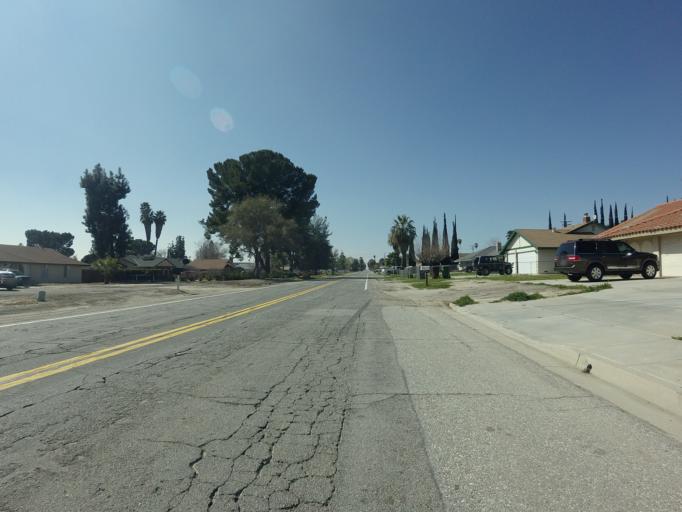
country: US
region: California
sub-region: Riverside County
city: Moreno Valley
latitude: 33.9175
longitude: -117.1537
